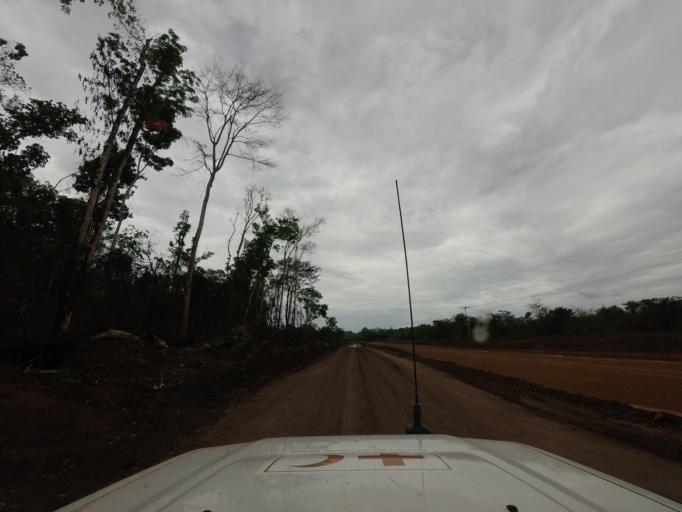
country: LR
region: Nimba
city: Sanniquellie
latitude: 7.2551
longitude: -8.8548
